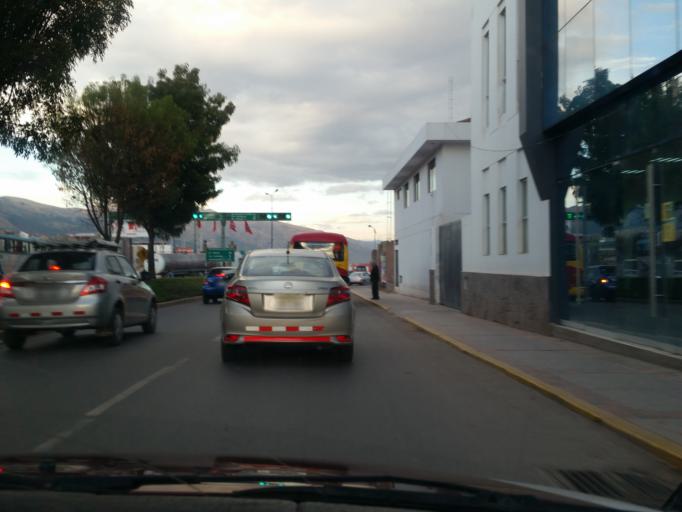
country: PE
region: Cusco
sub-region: Provincia de Cusco
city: Cusco
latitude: -13.5332
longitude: -71.9562
